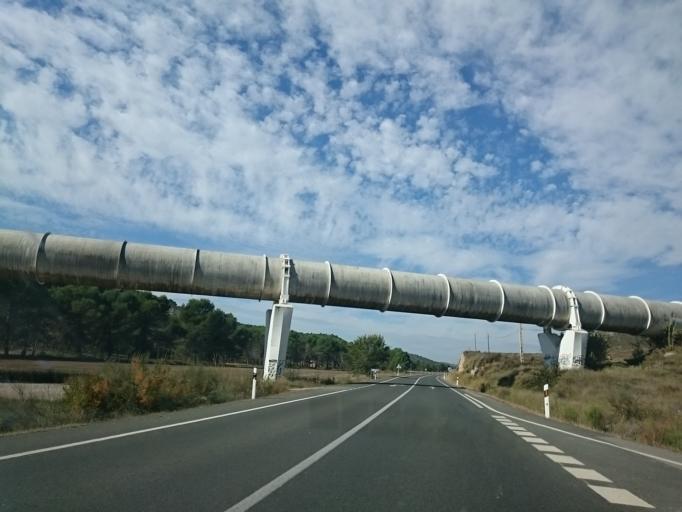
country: ES
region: Catalonia
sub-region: Provincia de Lleida
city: Alfarras
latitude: 41.8623
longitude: 0.5661
